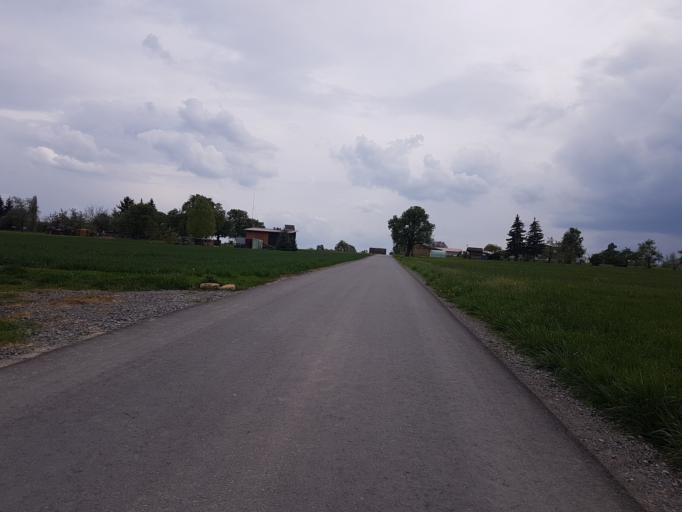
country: DE
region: Baden-Wuerttemberg
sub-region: Regierungsbezirk Stuttgart
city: Bondorf
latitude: 48.5254
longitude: 8.8221
